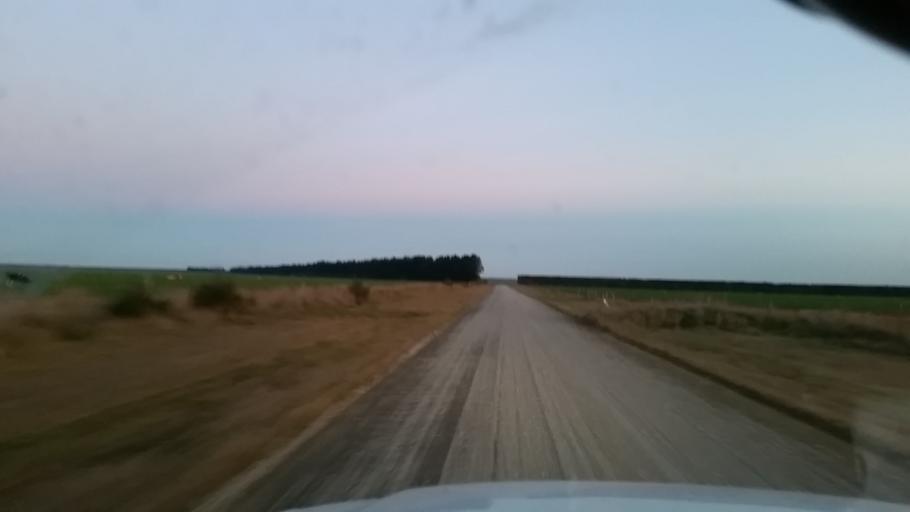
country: NZ
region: Canterbury
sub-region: Ashburton District
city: Tinwald
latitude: -43.9416
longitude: 171.6101
